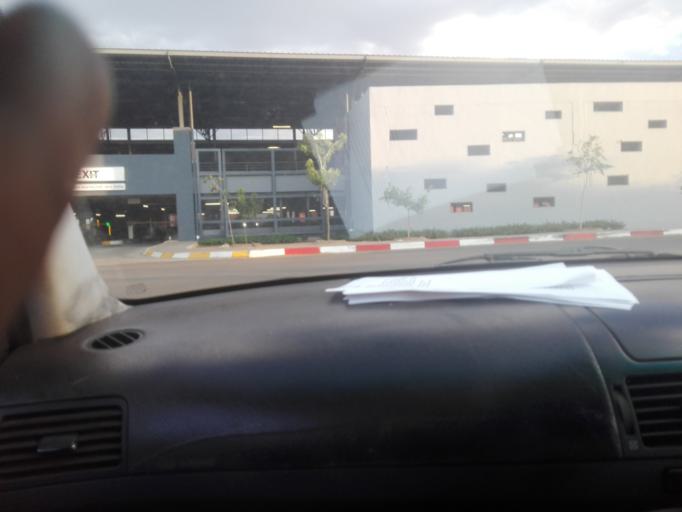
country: BW
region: South East
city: Gaborone
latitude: -24.6854
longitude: 25.8782
